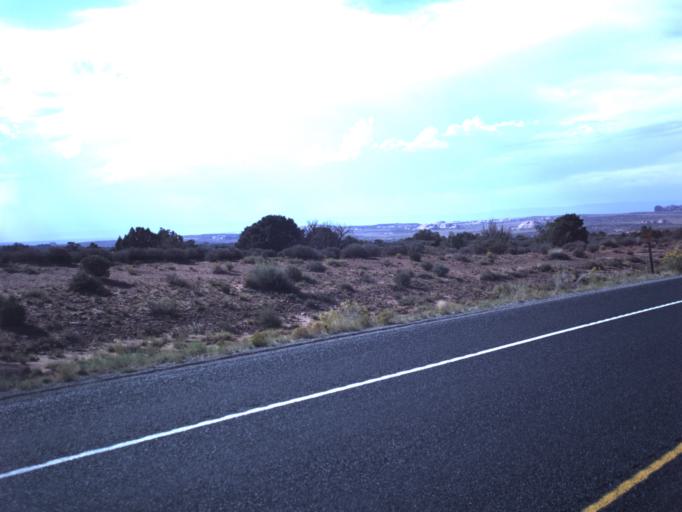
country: US
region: Utah
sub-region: Grand County
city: Moab
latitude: 38.6031
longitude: -109.8168
